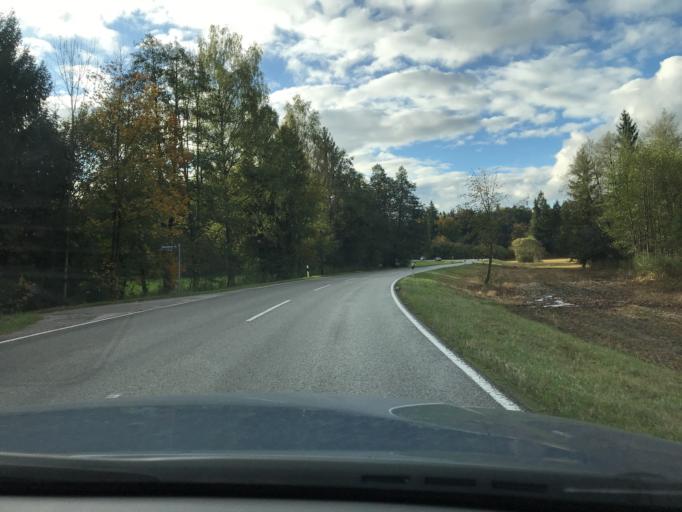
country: DE
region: Bavaria
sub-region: Upper Bavaria
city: Bad Toelz
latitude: 47.7809
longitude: 11.5548
